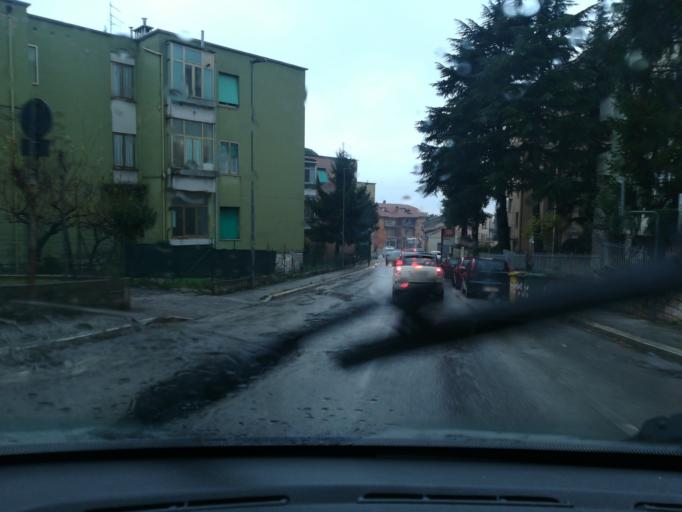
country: IT
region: The Marches
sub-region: Provincia di Macerata
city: Macerata
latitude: 43.2918
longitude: 13.4361
